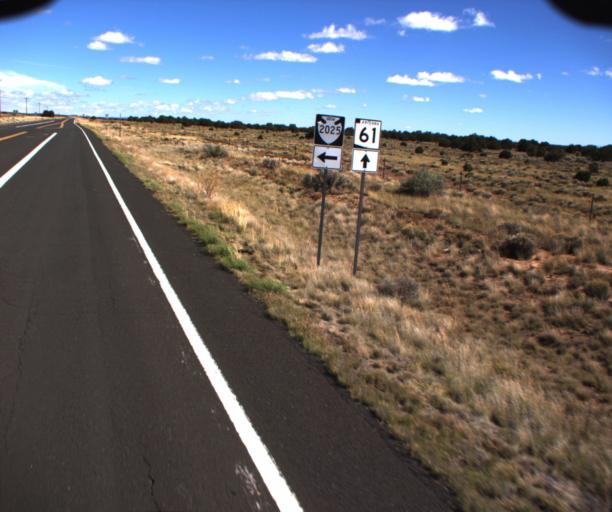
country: US
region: New Mexico
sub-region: McKinley County
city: Zuni Pueblo
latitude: 34.9658
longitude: -109.1493
